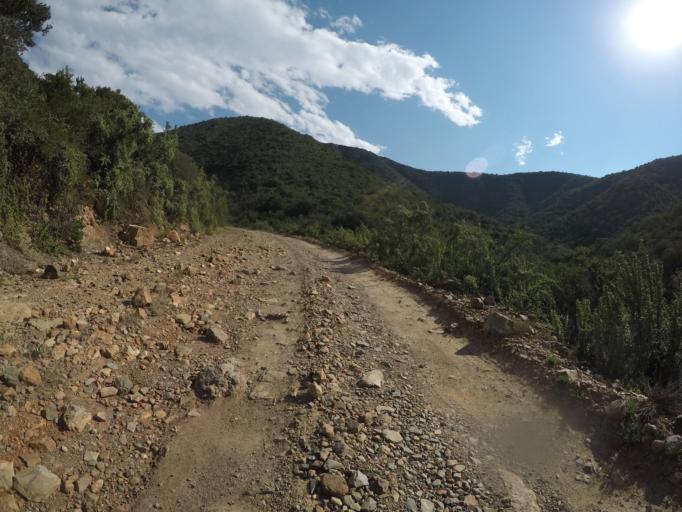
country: ZA
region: Eastern Cape
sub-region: Cacadu District Municipality
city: Kareedouw
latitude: -33.6529
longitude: 24.3502
